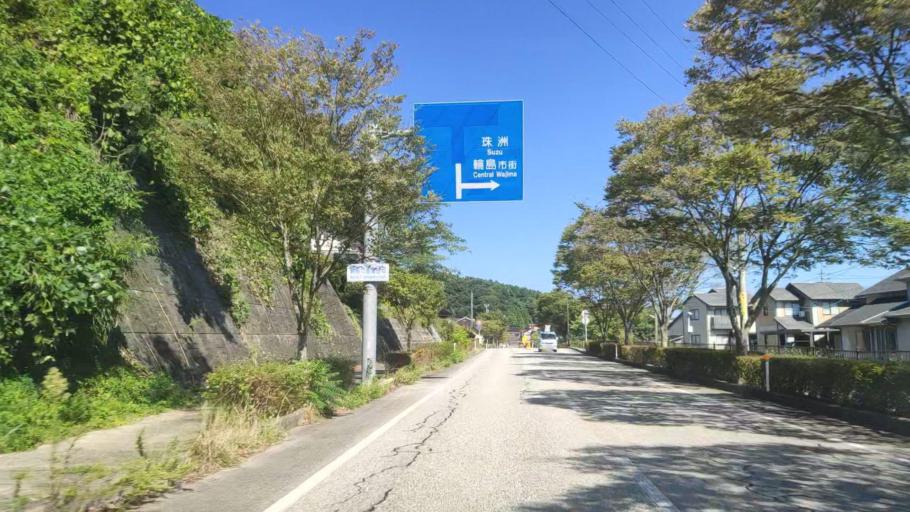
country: JP
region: Ishikawa
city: Nanao
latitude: 37.3923
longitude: 136.8927
